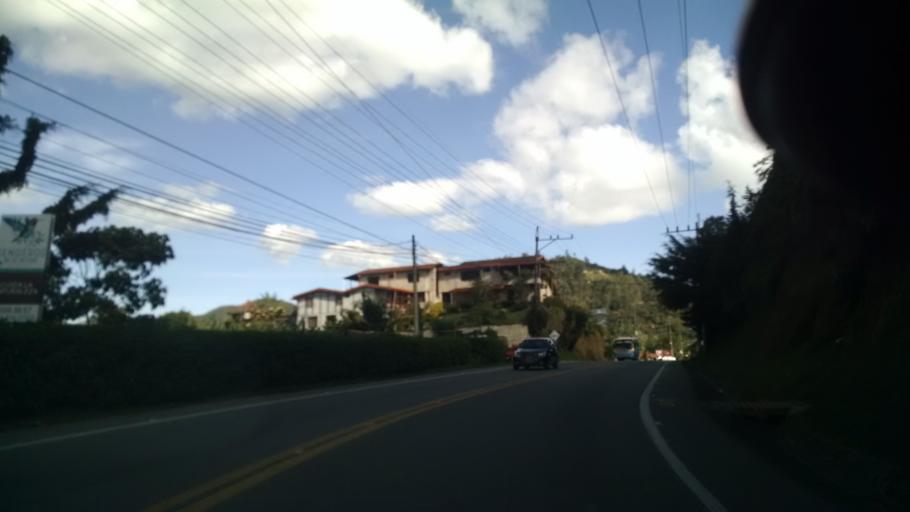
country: CO
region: Antioquia
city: El Retiro
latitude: 6.0935
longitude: -75.4851
